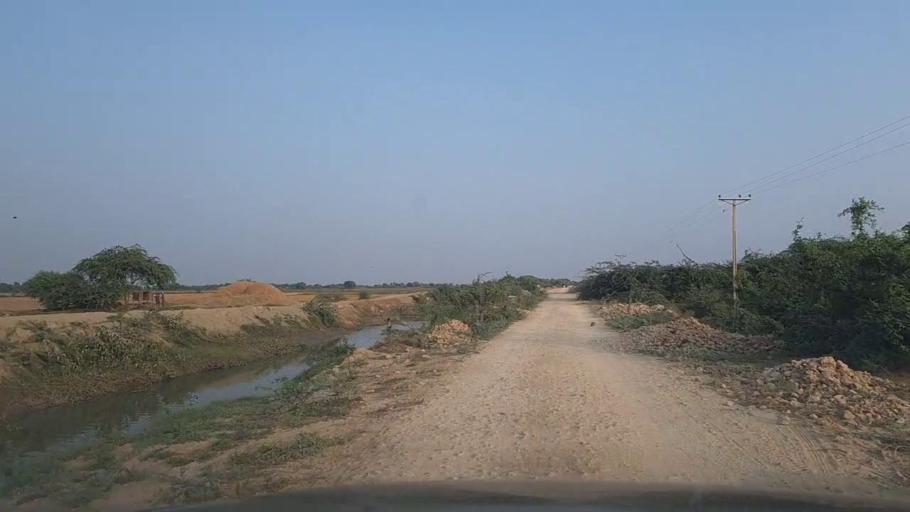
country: PK
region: Sindh
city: Mirpur Batoro
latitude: 24.5461
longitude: 68.3524
